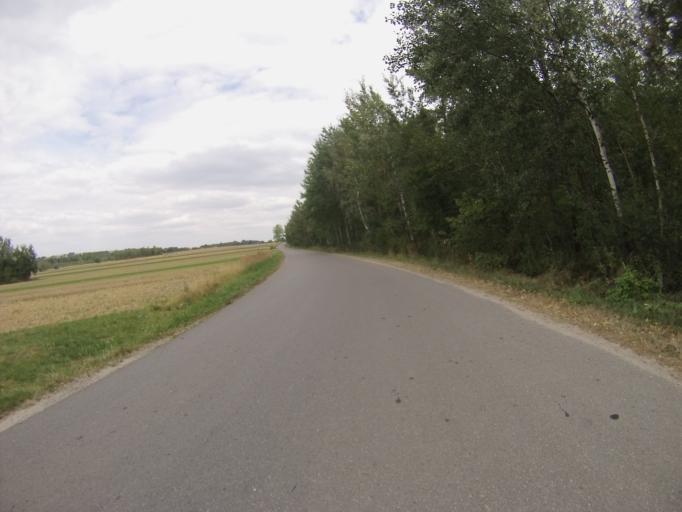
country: PL
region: Swietokrzyskie
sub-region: Powiat staszowski
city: Bogoria
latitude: 50.6815
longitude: 21.1911
